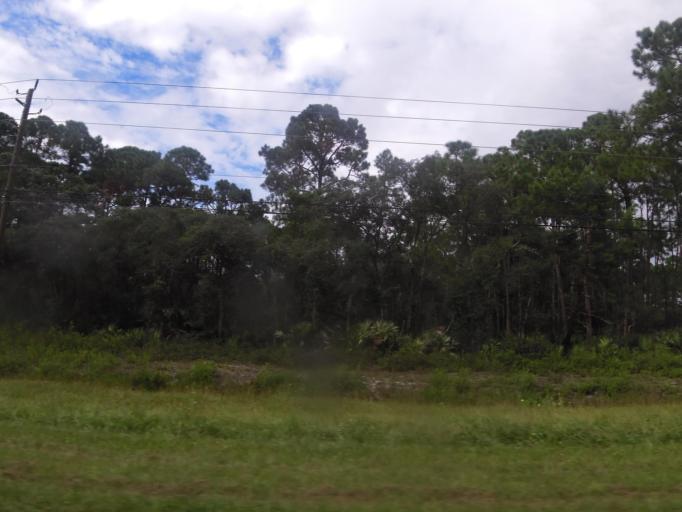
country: US
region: Florida
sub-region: Saint Johns County
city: Butler Beach
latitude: 29.7568
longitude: -81.2994
